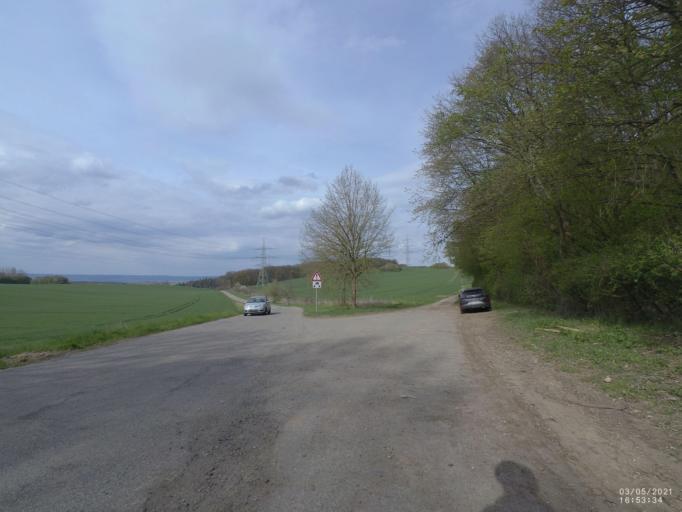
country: DE
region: Rheinland-Pfalz
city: Wolken
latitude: 50.3420
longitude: 7.4557
